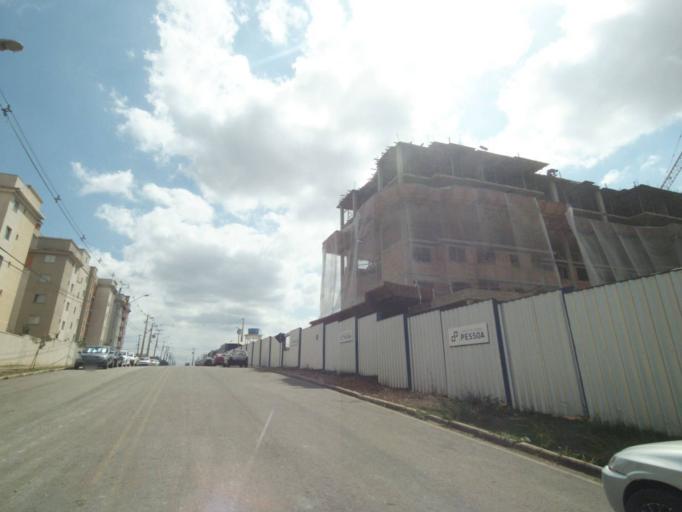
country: BR
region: Parana
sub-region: Curitiba
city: Curitiba
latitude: -25.5021
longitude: -49.3087
